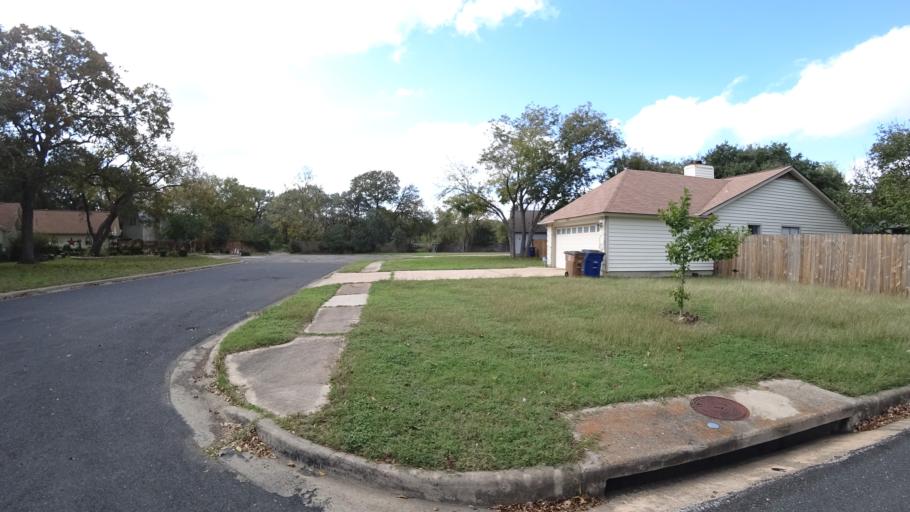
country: US
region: Texas
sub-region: Williamson County
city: Jollyville
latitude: 30.4296
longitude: -97.7288
